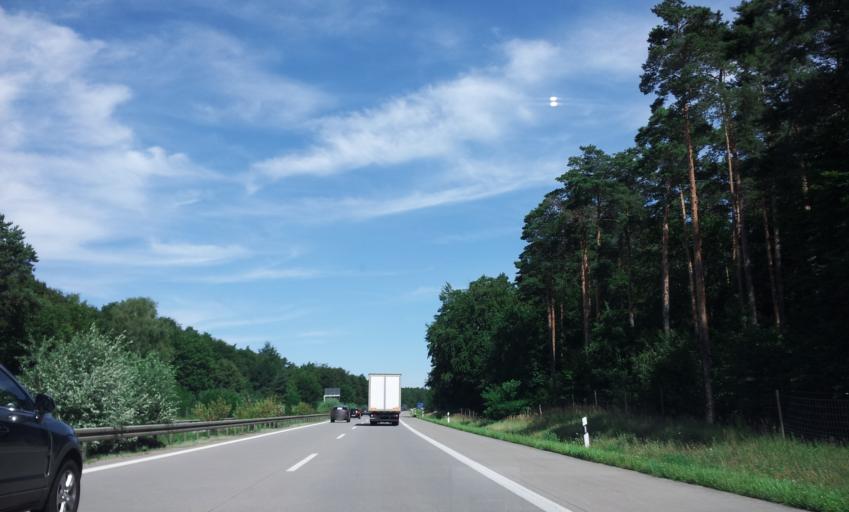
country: DE
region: Brandenburg
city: Bernau bei Berlin
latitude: 52.7293
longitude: 13.5405
